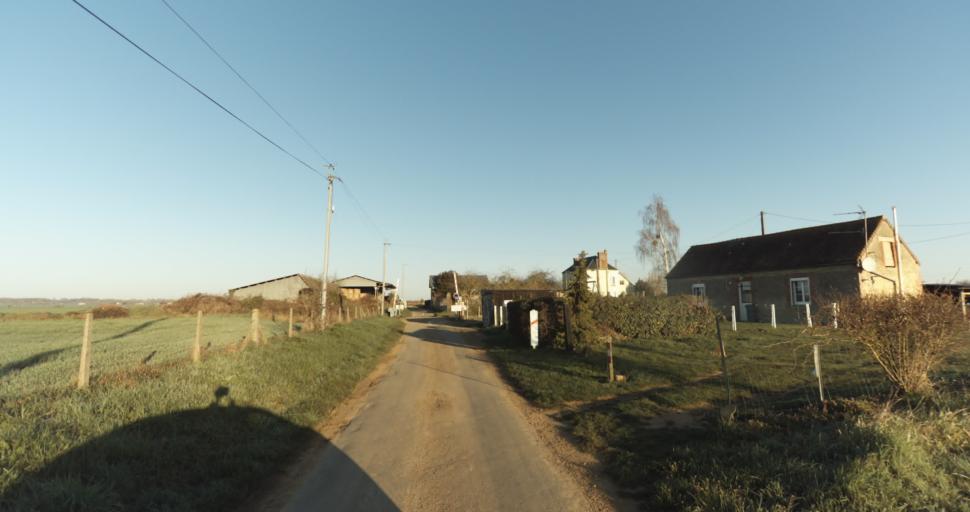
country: FR
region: Lower Normandy
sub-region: Departement du Calvados
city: Saint-Pierre-sur-Dives
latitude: 49.0321
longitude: -0.0340
